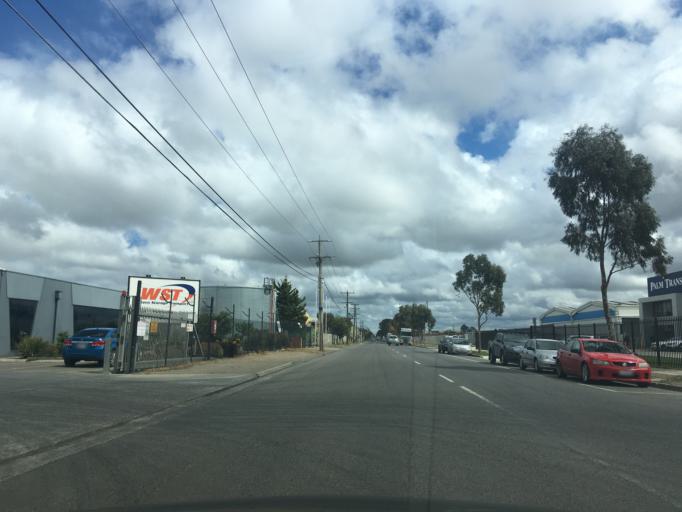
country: AU
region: Victoria
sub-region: Brimbank
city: Brooklyn
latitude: -37.8321
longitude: 144.8074
